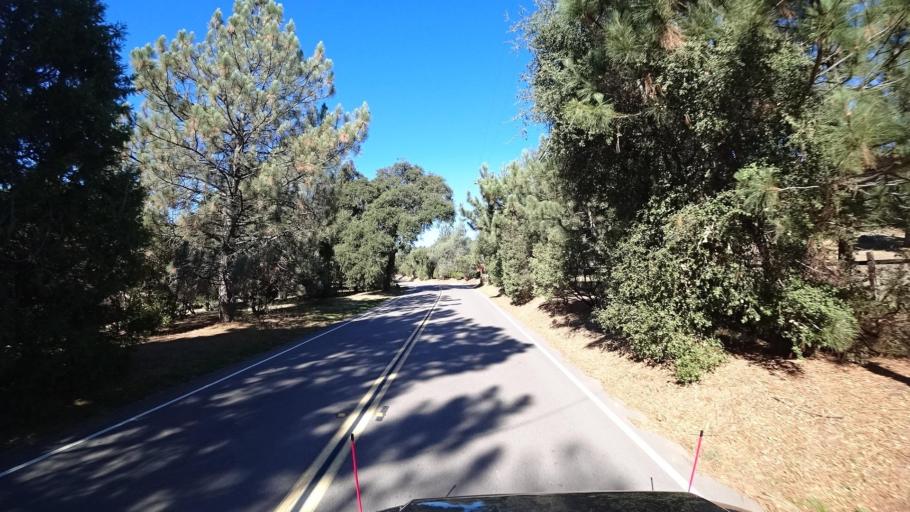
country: US
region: California
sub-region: San Diego County
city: Descanso
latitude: 32.8558
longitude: -116.6238
